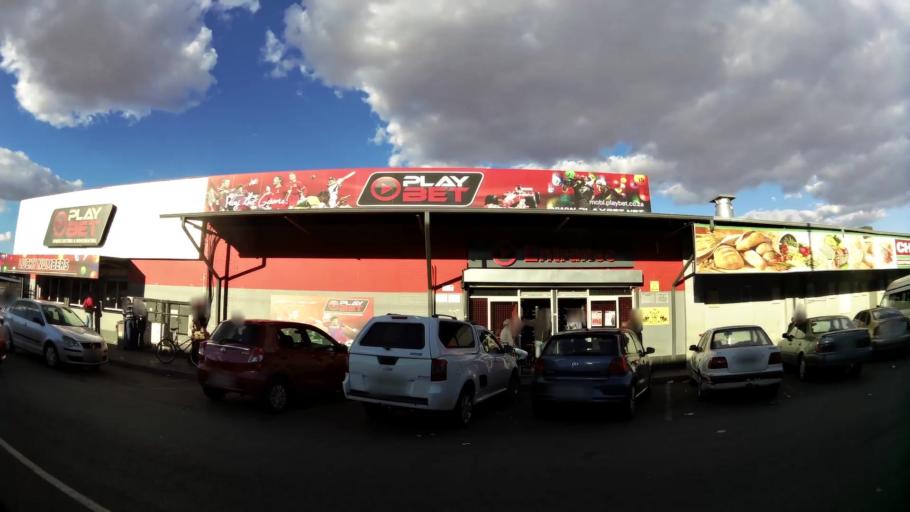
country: ZA
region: North-West
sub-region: Dr Kenneth Kaunda District Municipality
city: Potchefstroom
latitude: -26.7116
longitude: 27.1011
